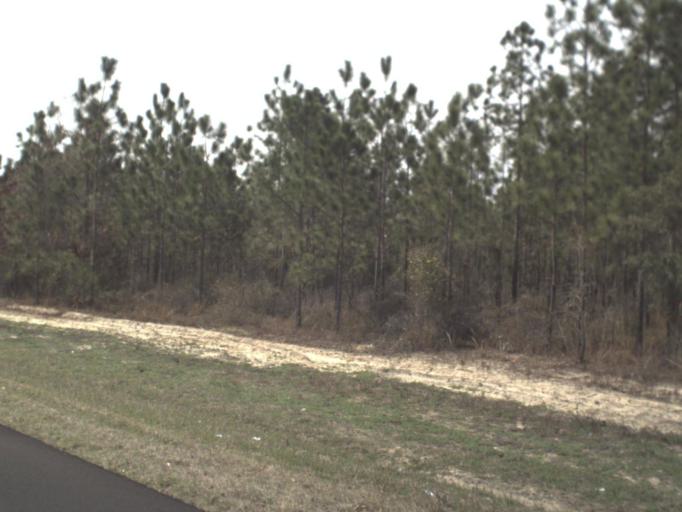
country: US
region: Florida
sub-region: Gadsden County
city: Midway
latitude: 30.4412
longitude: -84.4860
